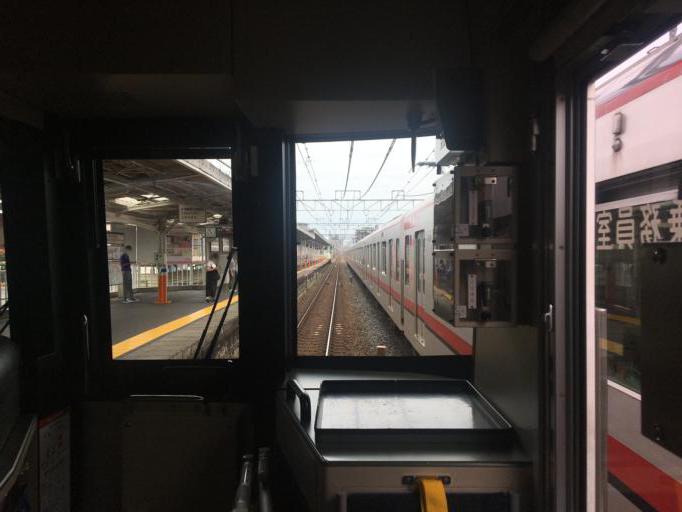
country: JP
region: Saitama
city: Kasukabe
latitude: 35.9617
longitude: 139.7668
